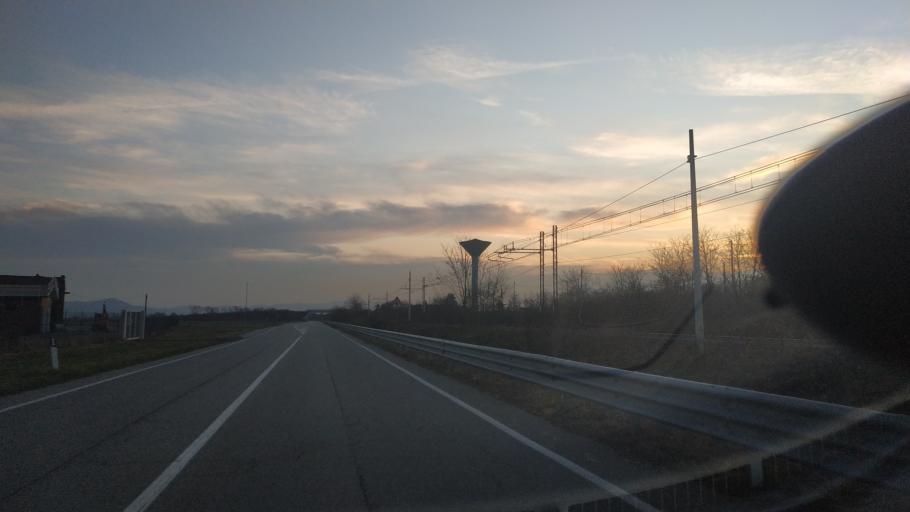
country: IT
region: Piedmont
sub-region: Provincia di Torino
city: Montanaro
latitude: 45.2472
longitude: 7.8636
